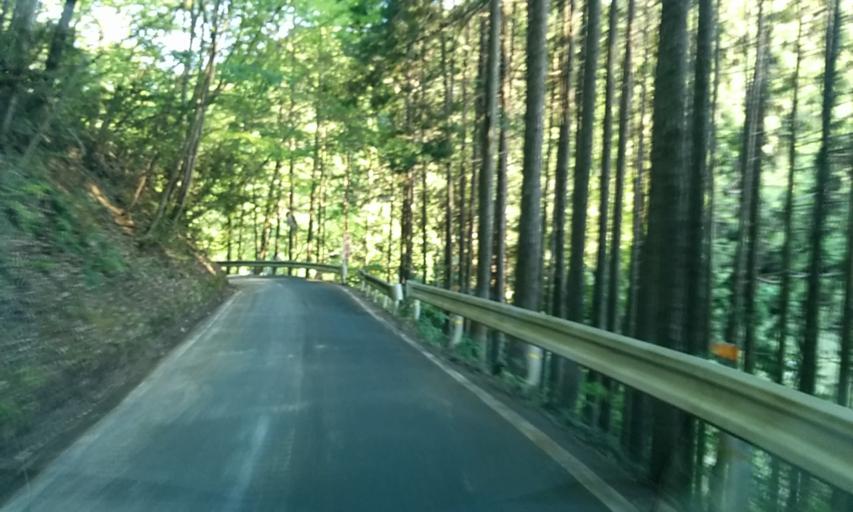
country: JP
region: Kyoto
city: Kameoka
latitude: 35.1134
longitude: 135.4317
